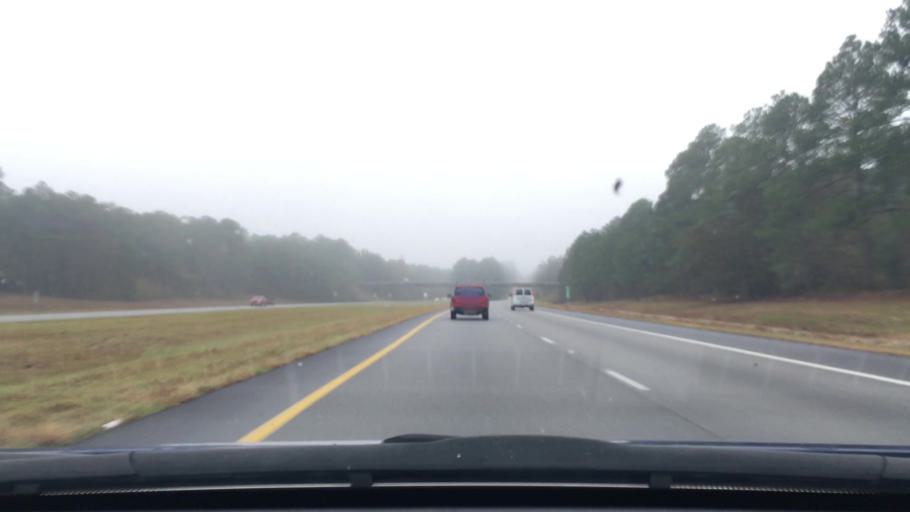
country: US
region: South Carolina
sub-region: Kershaw County
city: Camden
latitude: 34.2082
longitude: -80.4502
